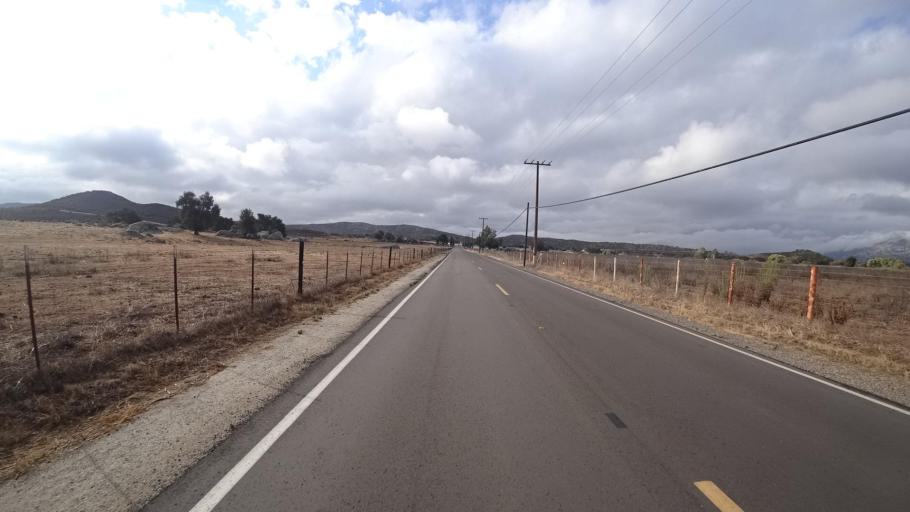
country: MX
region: Baja California
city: Tecate
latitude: 32.6190
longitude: -116.6134
